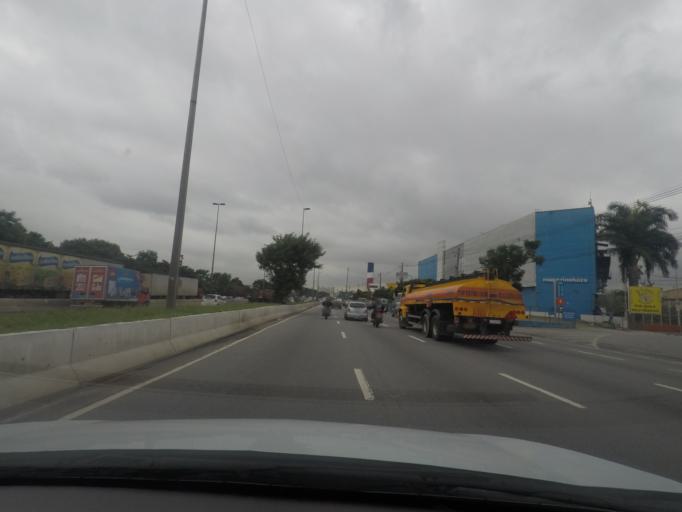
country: BR
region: Sao Paulo
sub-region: Sao Paulo
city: Sao Paulo
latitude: -23.5217
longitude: -46.6130
